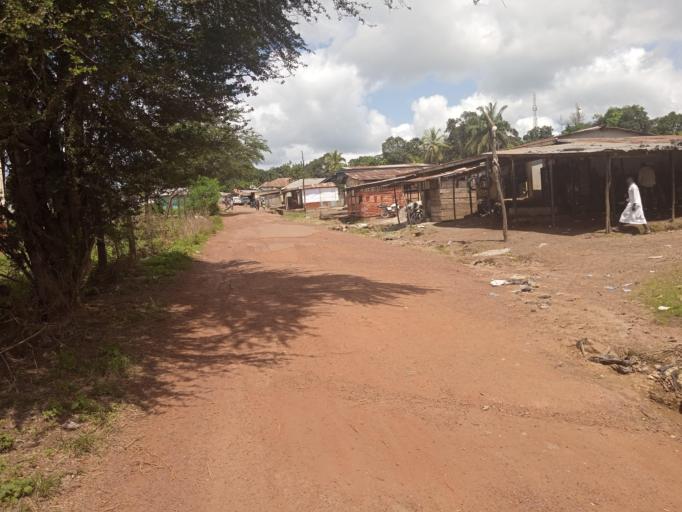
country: SL
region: Northern Province
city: Kamakwie
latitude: 9.4977
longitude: -12.2422
